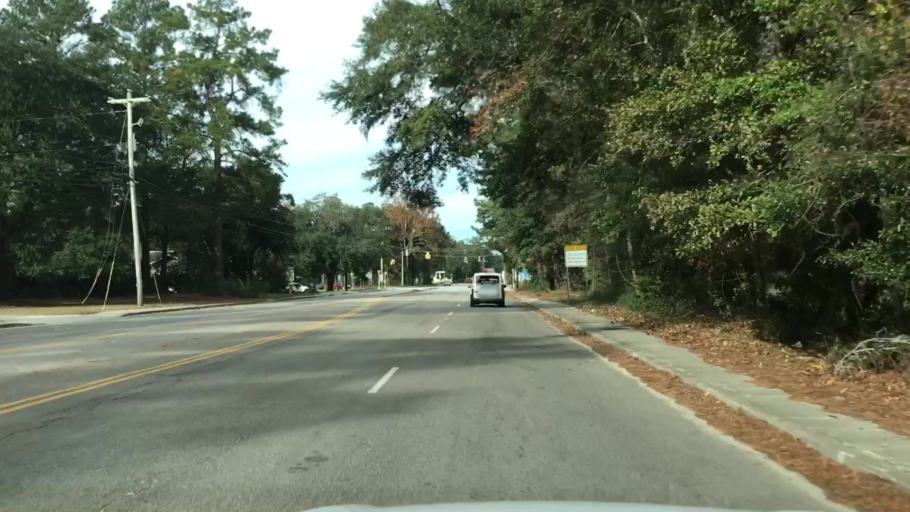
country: US
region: South Carolina
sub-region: Colleton County
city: Walterboro
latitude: 32.8973
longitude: -80.6460
